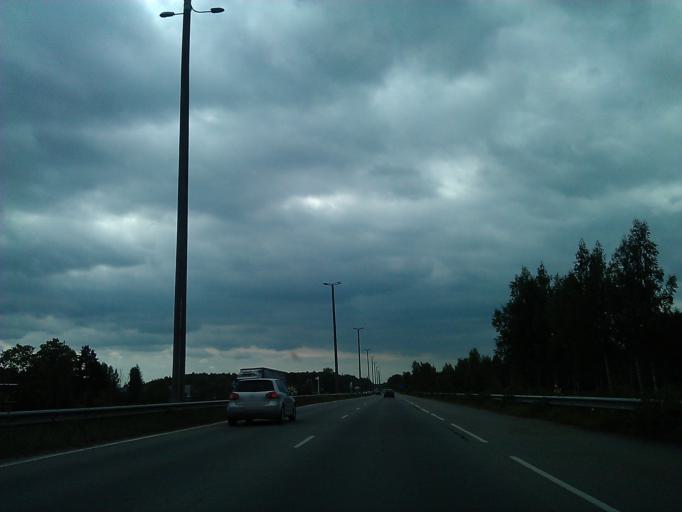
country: LV
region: Marupe
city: Marupe
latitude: 56.8864
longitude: 24.0744
